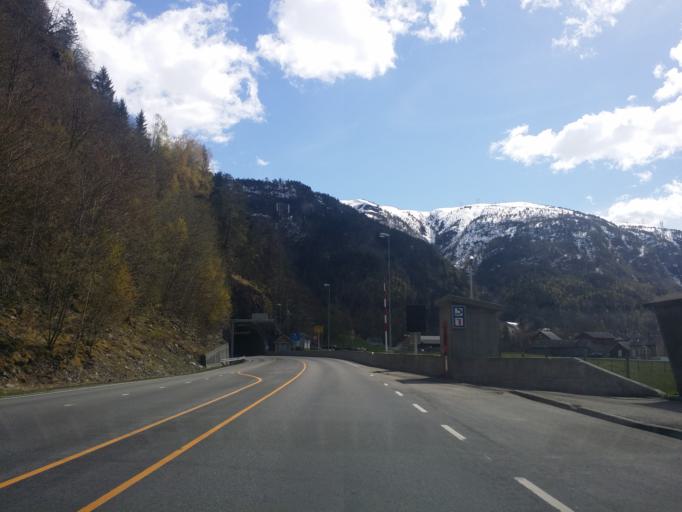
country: NO
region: Hordaland
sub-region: Granvin
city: Granvin
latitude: 60.5342
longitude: 6.7344
